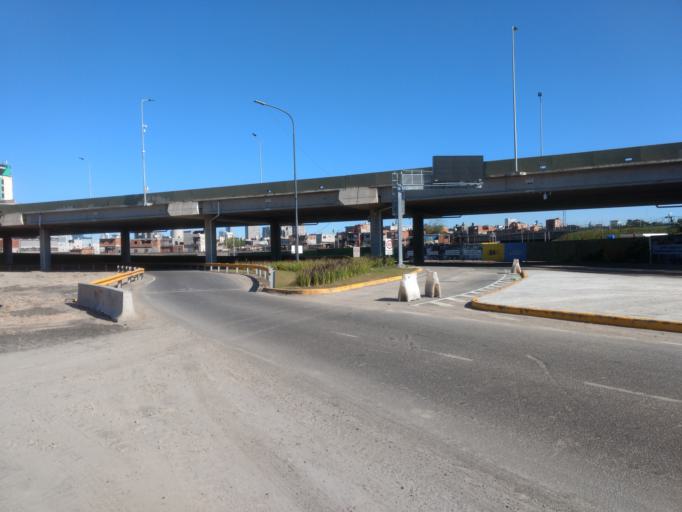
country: AR
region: Buenos Aires F.D.
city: Retiro
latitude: -34.5767
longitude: -58.3888
